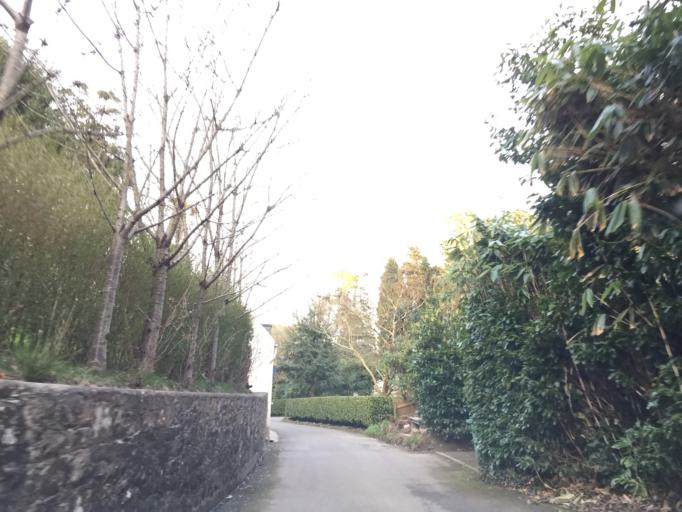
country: JE
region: St Helier
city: Saint Helier
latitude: 49.2338
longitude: -2.0502
